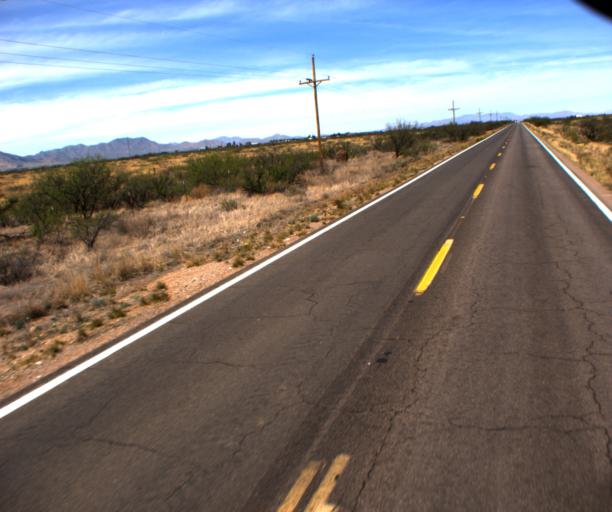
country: US
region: Arizona
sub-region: Cochise County
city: Tombstone
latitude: 31.9125
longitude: -109.8171
